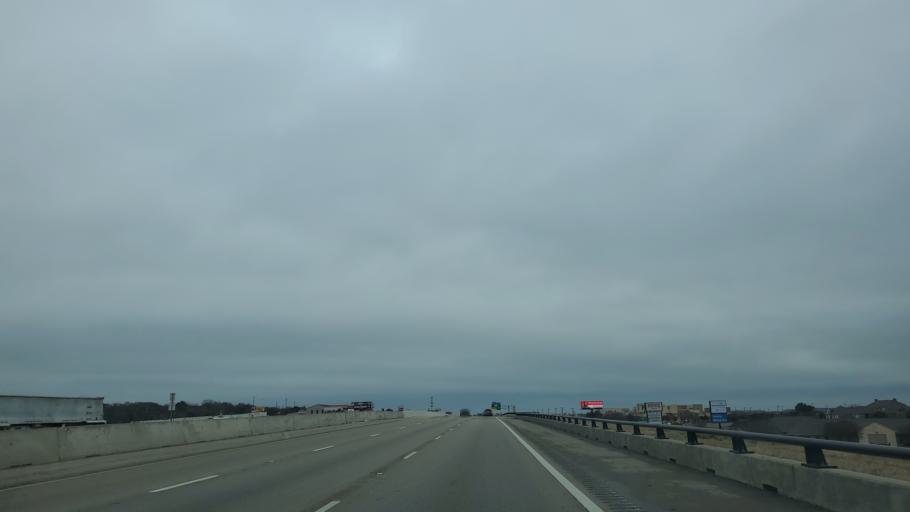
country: US
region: Texas
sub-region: Bell County
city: Harker Heights
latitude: 31.0765
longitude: -97.6899
